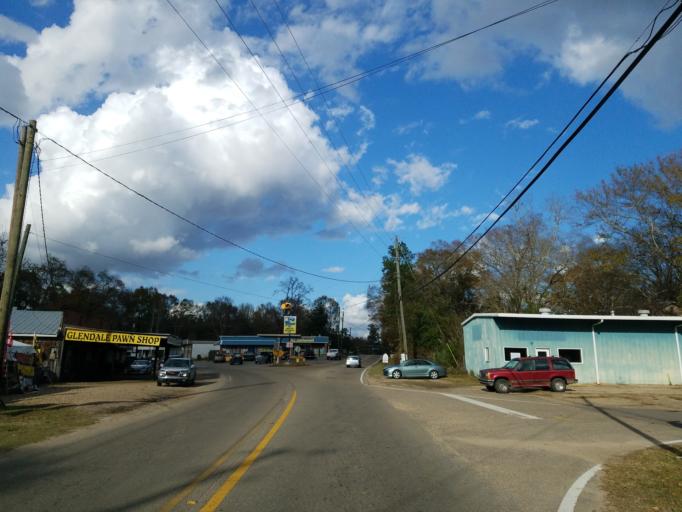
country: US
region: Mississippi
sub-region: Forrest County
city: Glendale
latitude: 31.3590
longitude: -89.3008
